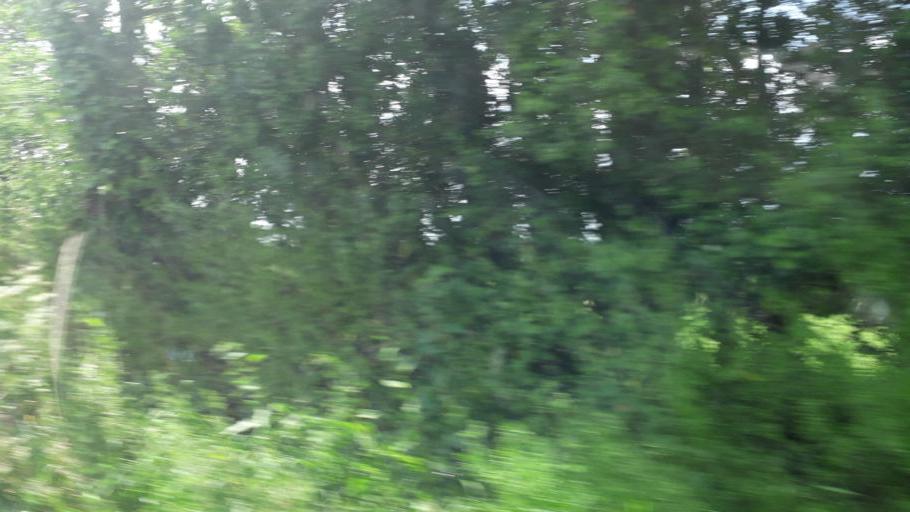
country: IE
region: Leinster
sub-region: Kilkenny
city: Graiguenamanagh
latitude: 52.6046
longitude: -6.9955
